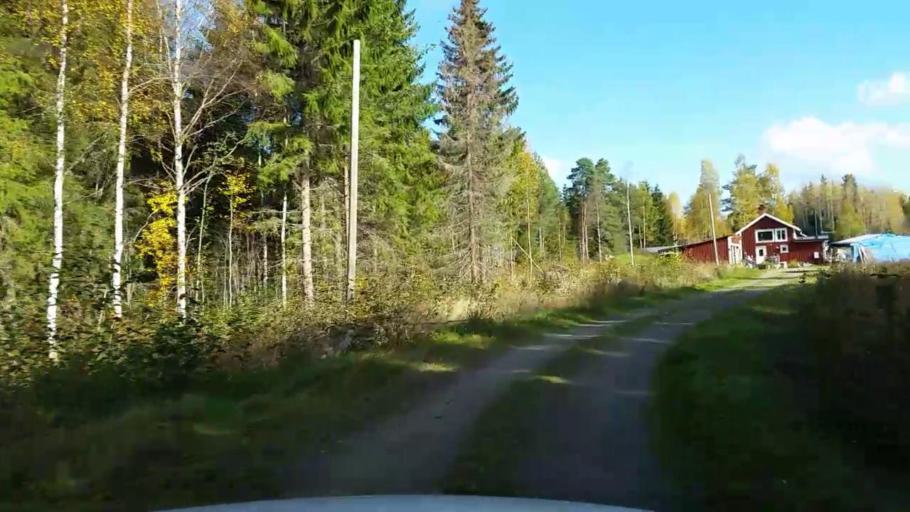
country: SE
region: Gaevleborg
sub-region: Ljusdals Kommun
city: Jaervsoe
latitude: 61.7892
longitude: 16.1568
